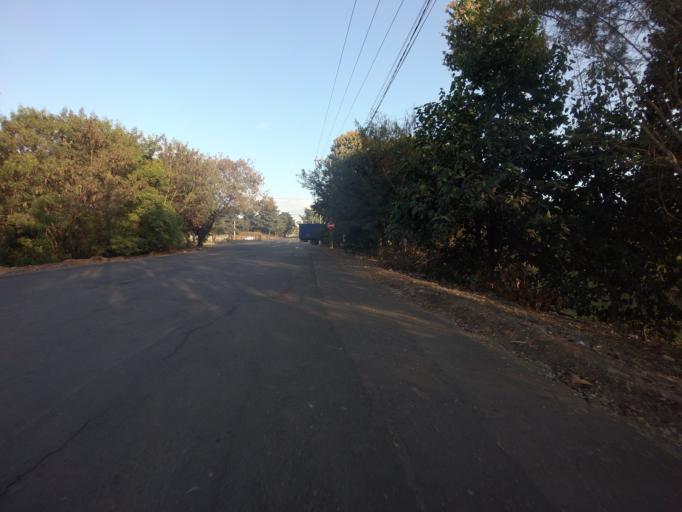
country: BR
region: Sao Paulo
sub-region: Piracicaba
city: Piracicaba
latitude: -22.7331
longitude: -47.5928
